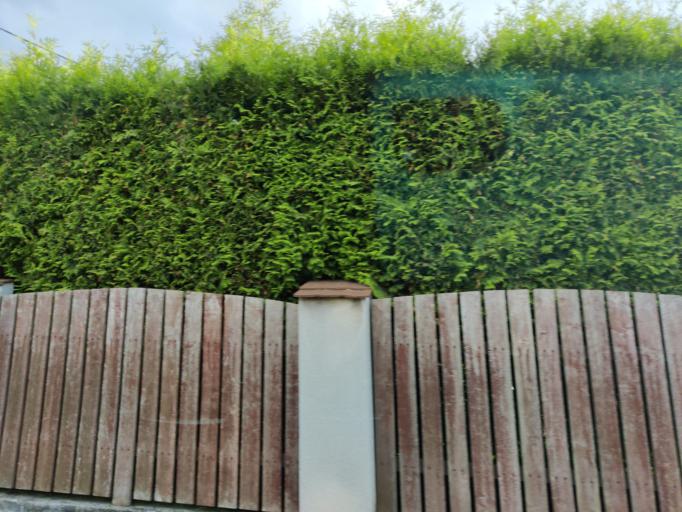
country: PL
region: Masovian Voivodeship
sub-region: Powiat piaseczynski
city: Konstancin-Jeziorna
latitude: 52.1183
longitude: 21.1062
